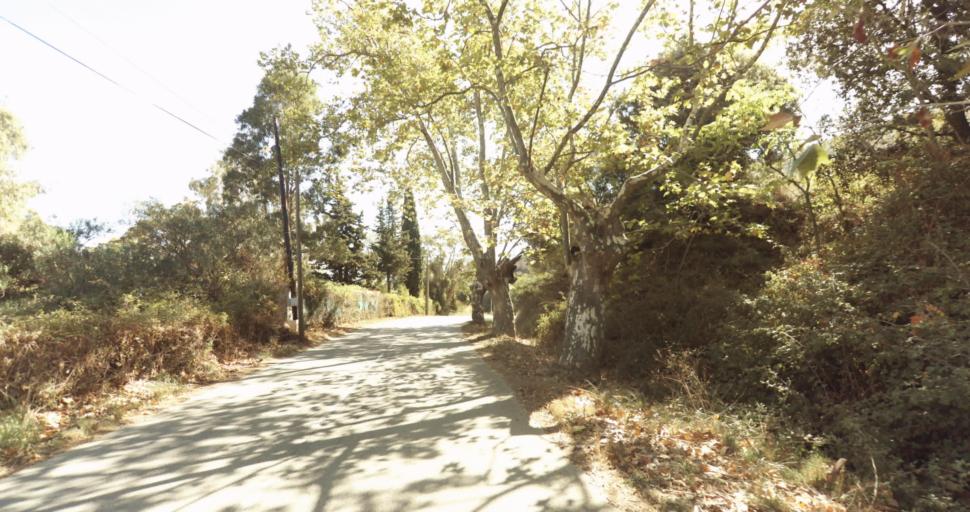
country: FR
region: Corsica
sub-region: Departement de la Corse-du-Sud
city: Ajaccio
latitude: 41.9288
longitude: 8.7002
